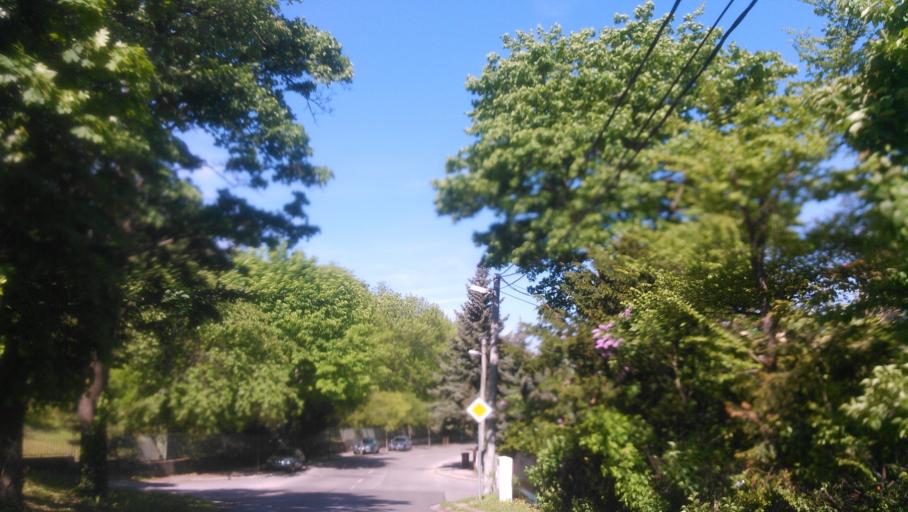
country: SK
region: Bratislavsky
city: Bratislava
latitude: 48.1607
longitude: 17.0930
